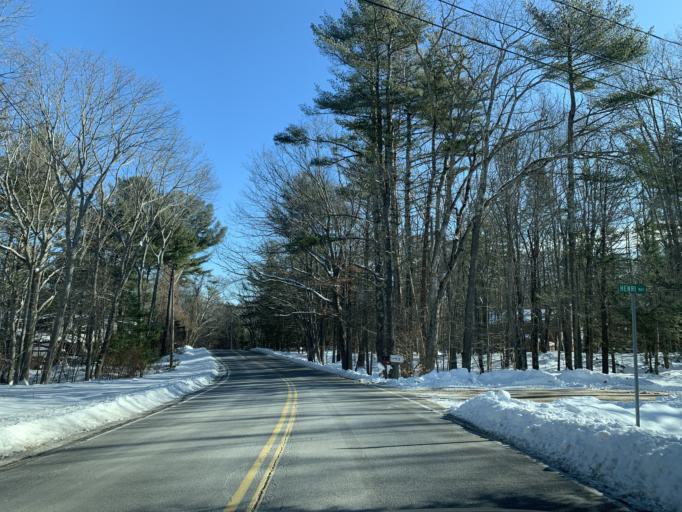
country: US
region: Maine
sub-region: York County
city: Ogunquit
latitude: 43.2482
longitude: -70.6232
